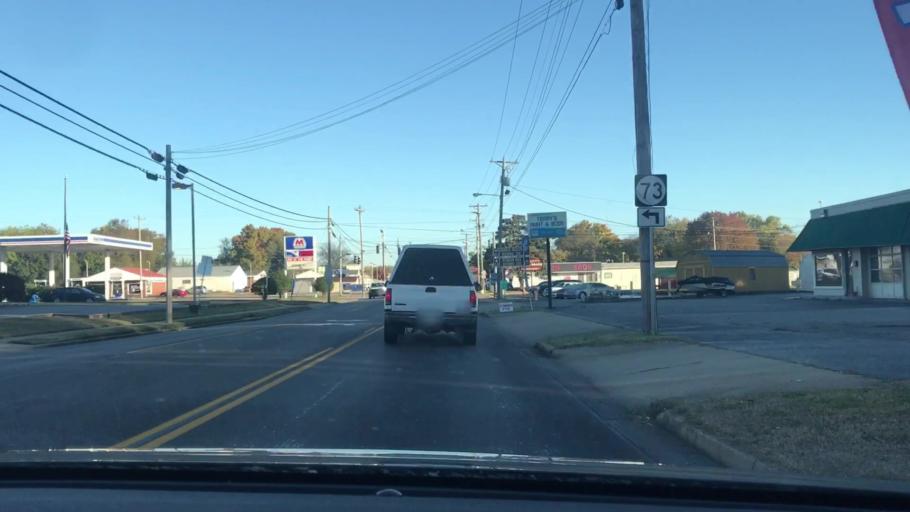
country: US
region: Kentucky
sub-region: Simpson County
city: Franklin
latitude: 36.7300
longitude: -86.5784
